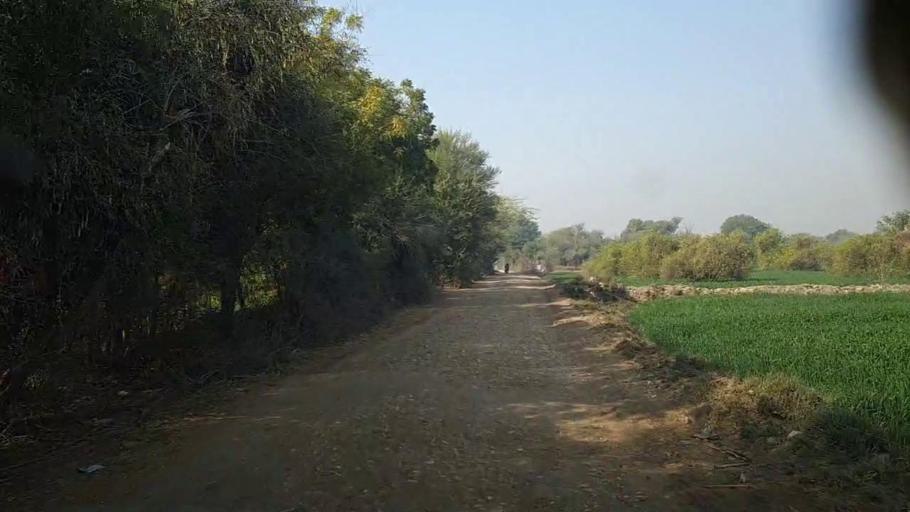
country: PK
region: Sindh
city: Karaundi
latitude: 26.8459
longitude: 68.3767
